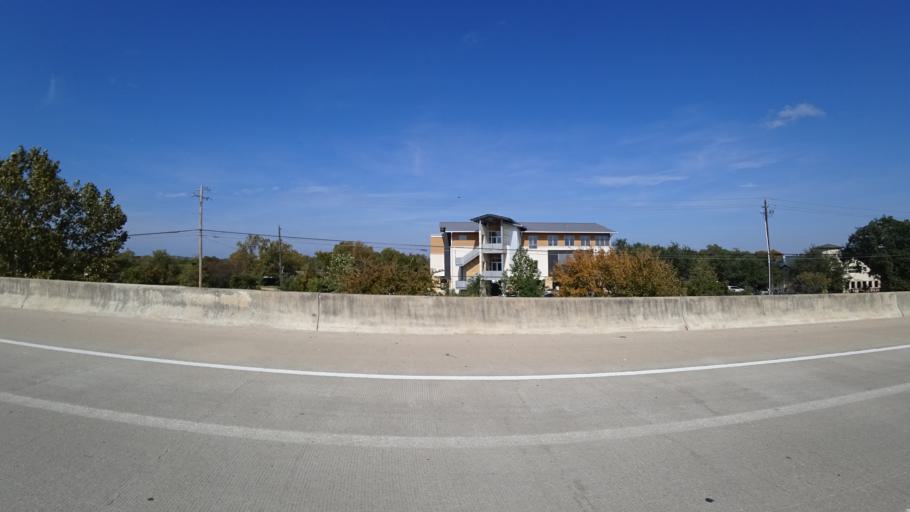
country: US
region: Texas
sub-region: Travis County
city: Rollingwood
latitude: 30.2336
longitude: -97.8143
